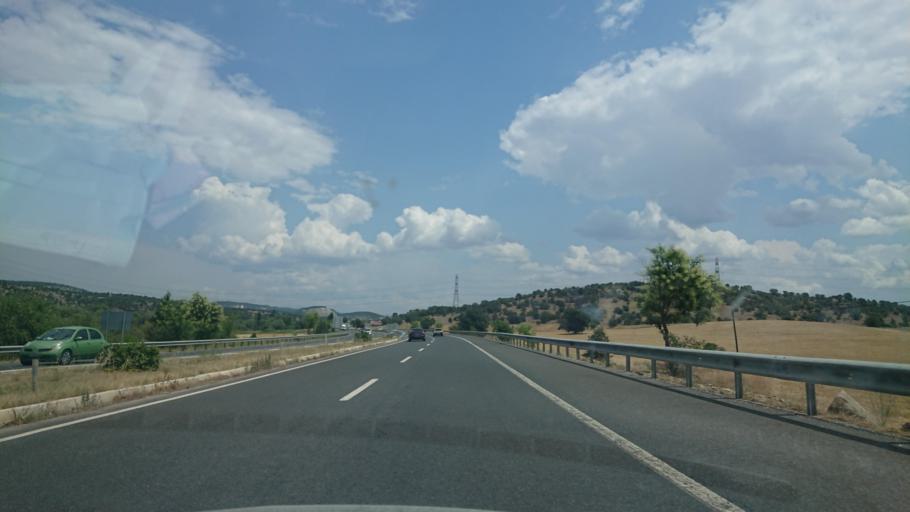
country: TR
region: Usak
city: Gure
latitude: 38.6591
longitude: 29.0579
